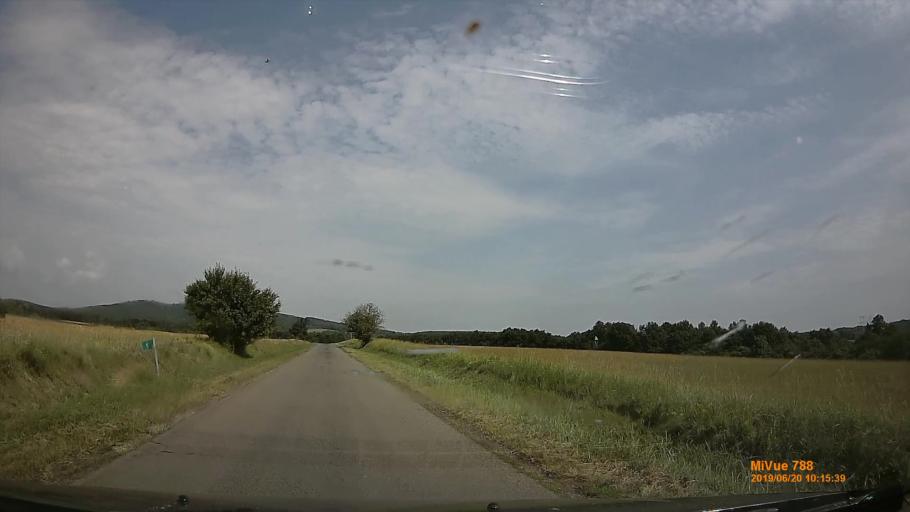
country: HU
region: Baranya
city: Mecseknadasd
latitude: 46.1935
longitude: 18.4637
